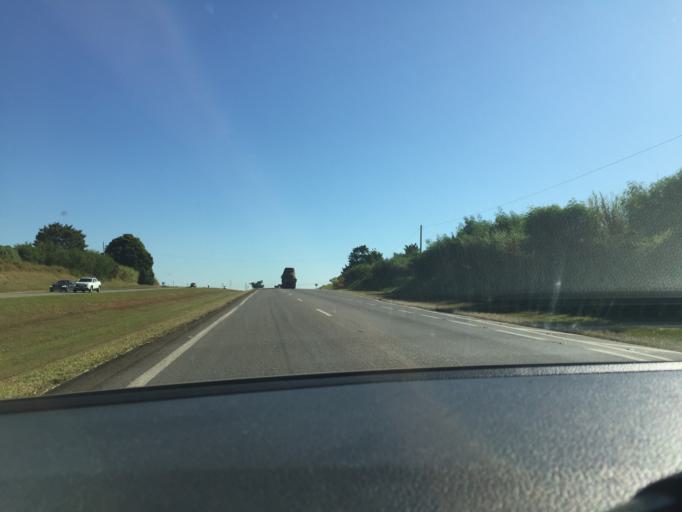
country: BR
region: Sao Paulo
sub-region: Santo Antonio De Posse
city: Santo Antonio de Posse
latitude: -22.5504
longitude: -46.9987
